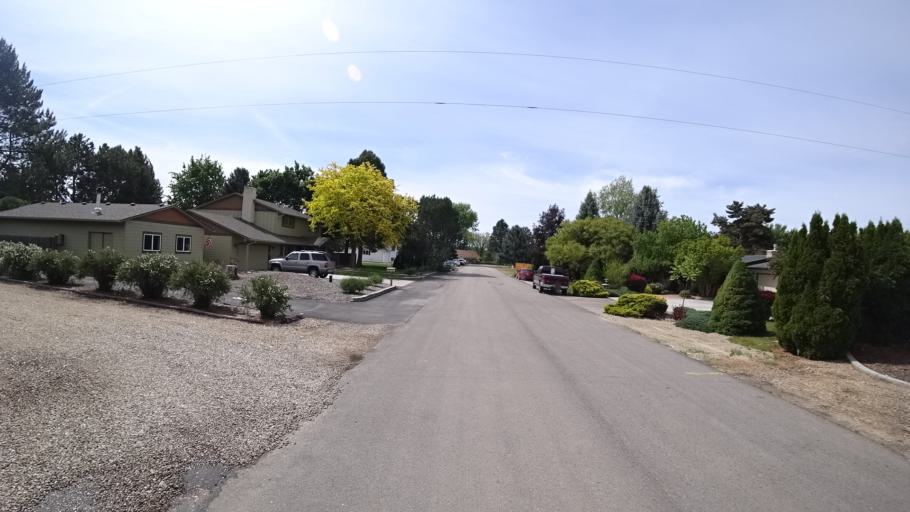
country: US
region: Idaho
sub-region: Ada County
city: Meridian
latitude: 43.5813
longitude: -116.3169
